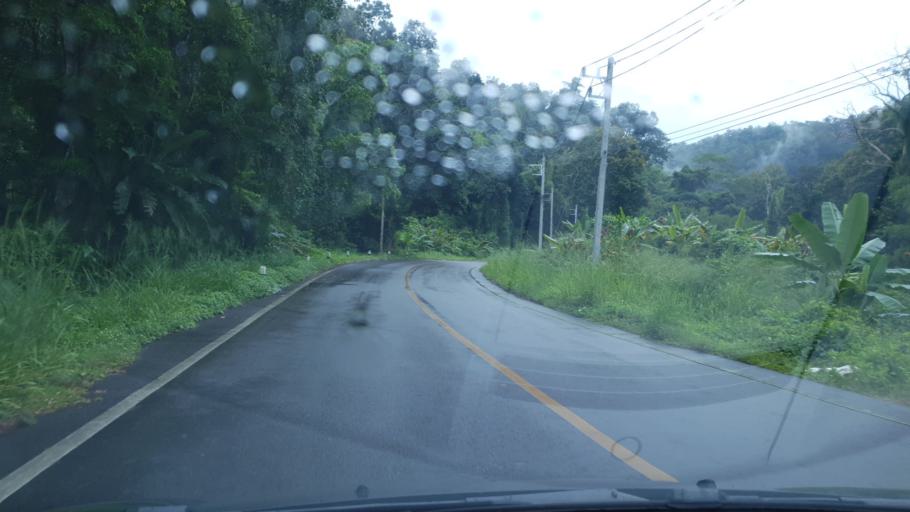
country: TH
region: Mae Hong Son
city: Mae La Noi
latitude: 18.6111
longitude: 97.9432
